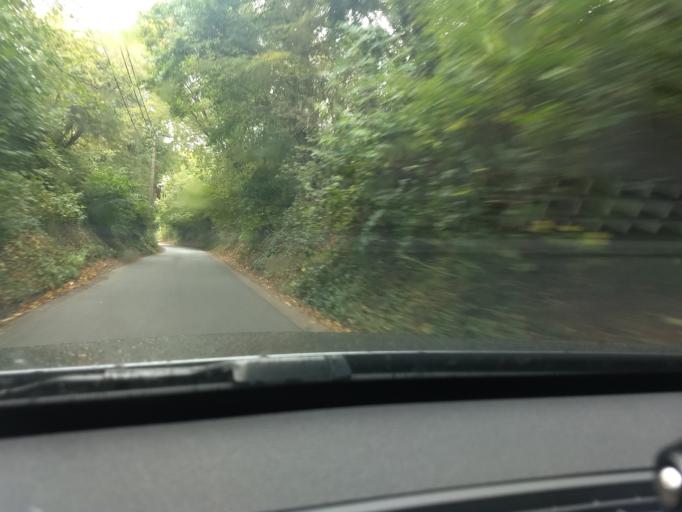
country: BE
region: Wallonia
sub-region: Province du Brabant Wallon
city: Braine-l'Alleud
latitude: 50.6720
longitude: 4.3730
